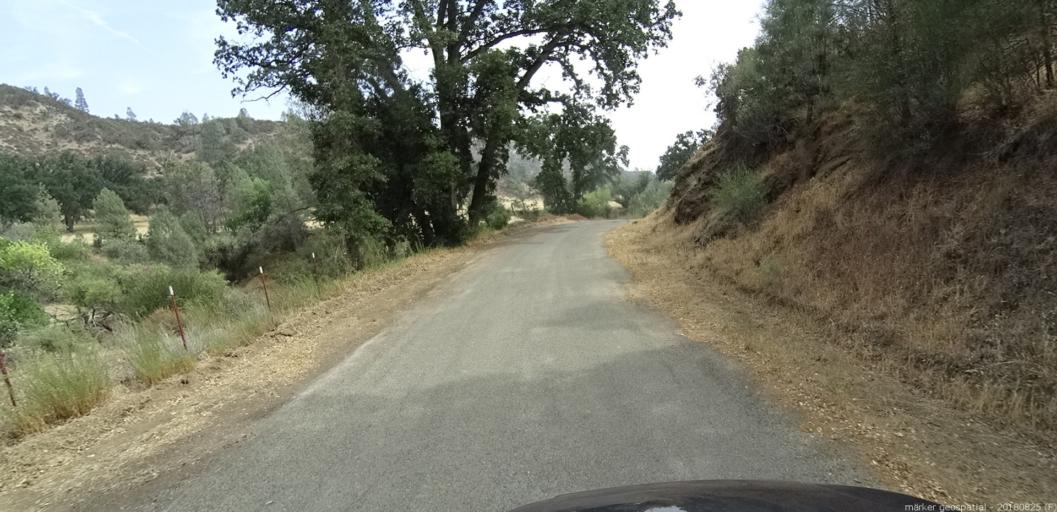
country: US
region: California
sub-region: Fresno County
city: Coalinga
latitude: 36.2250
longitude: -120.7073
